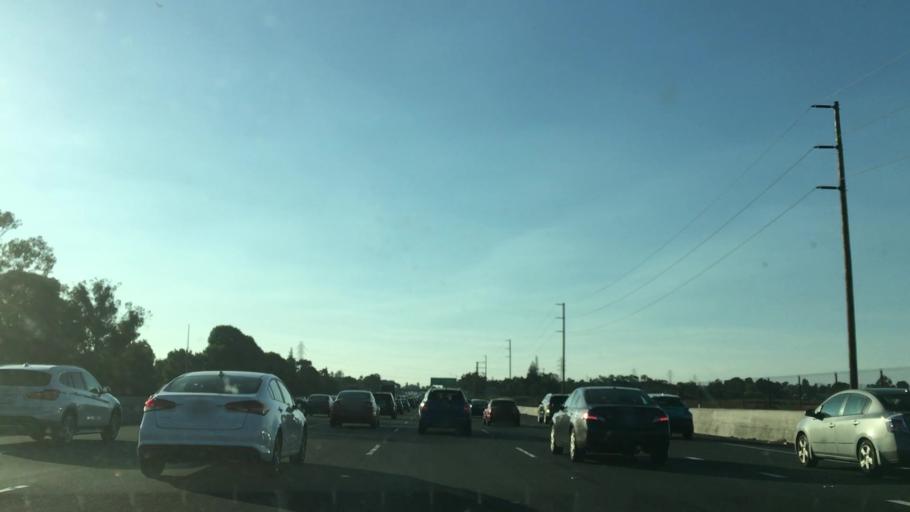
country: US
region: California
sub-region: Santa Clara County
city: Palo Alto
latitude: 37.4417
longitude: -122.1127
